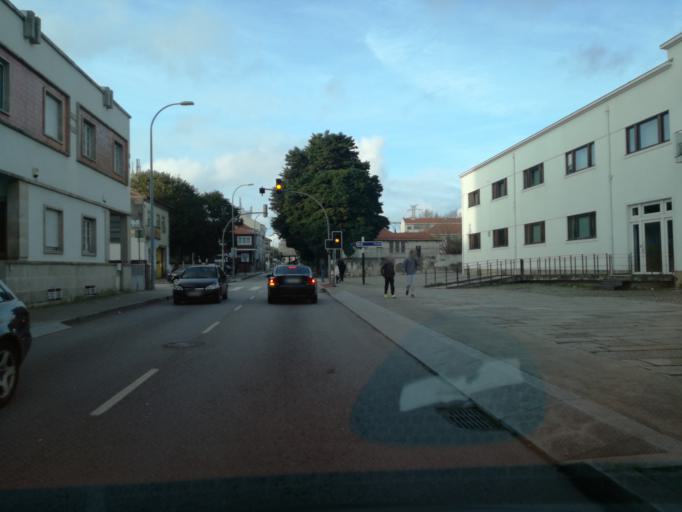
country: PT
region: Porto
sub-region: Porto
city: Porto
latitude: 41.1695
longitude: -8.6257
